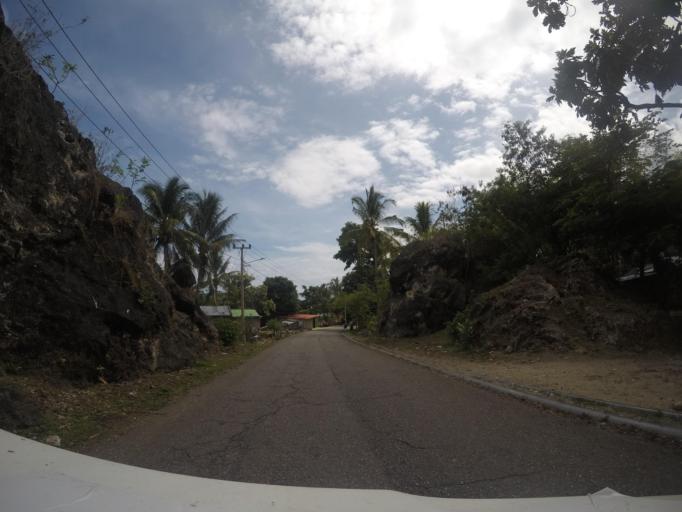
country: TL
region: Baucau
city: Baucau
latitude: -8.4623
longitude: 126.4390
